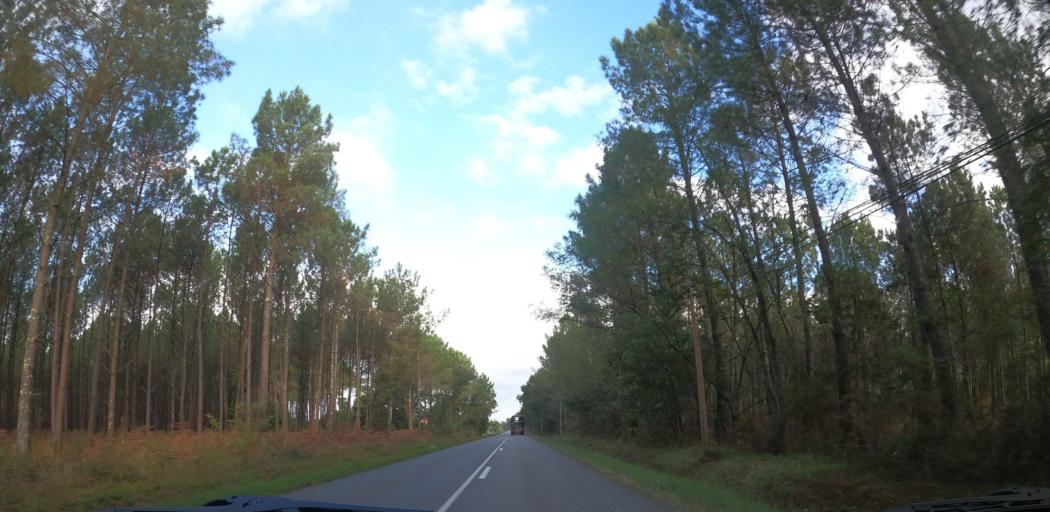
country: FR
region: Aquitaine
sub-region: Departement des Landes
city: Soustons
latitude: 43.7384
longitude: -1.2962
